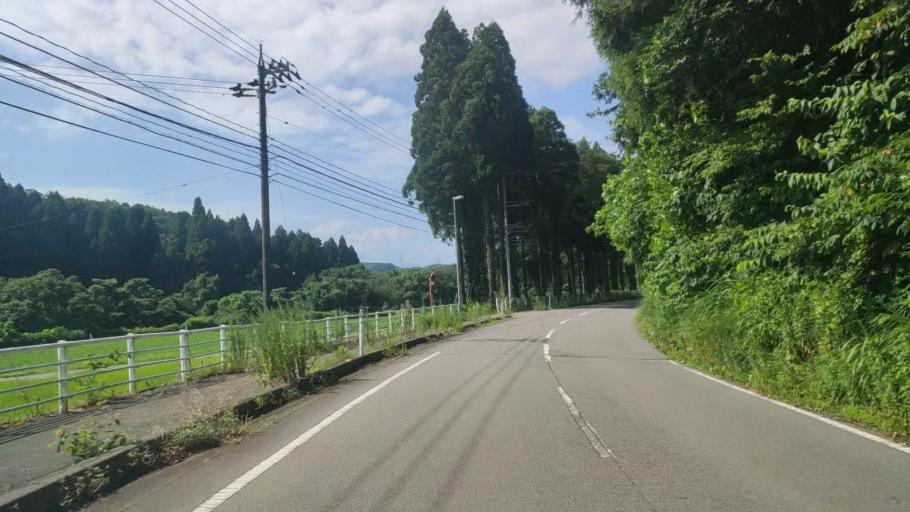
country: JP
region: Ishikawa
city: Komatsu
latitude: 36.3632
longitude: 136.4949
